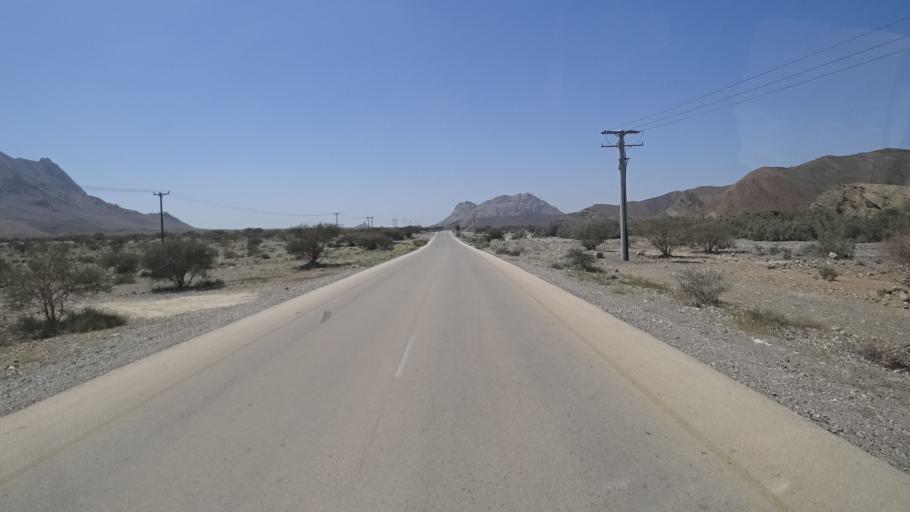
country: OM
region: Az Zahirah
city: `Ibri
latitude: 23.1968
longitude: 56.9349
